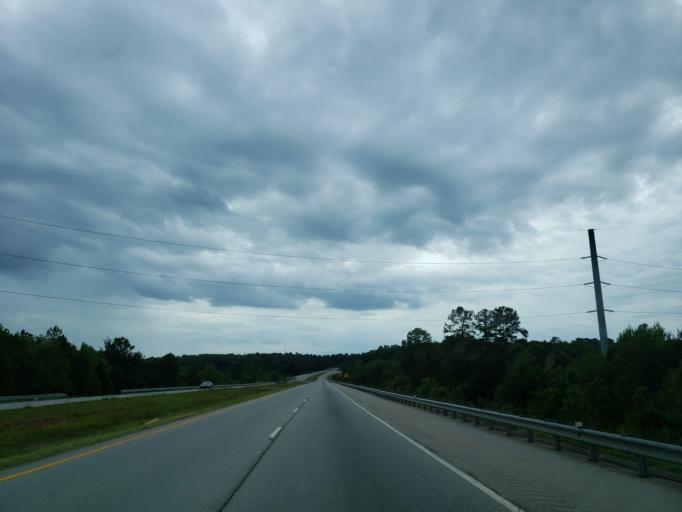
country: US
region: Georgia
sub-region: Polk County
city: Cedartown
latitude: 34.0076
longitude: -85.2222
